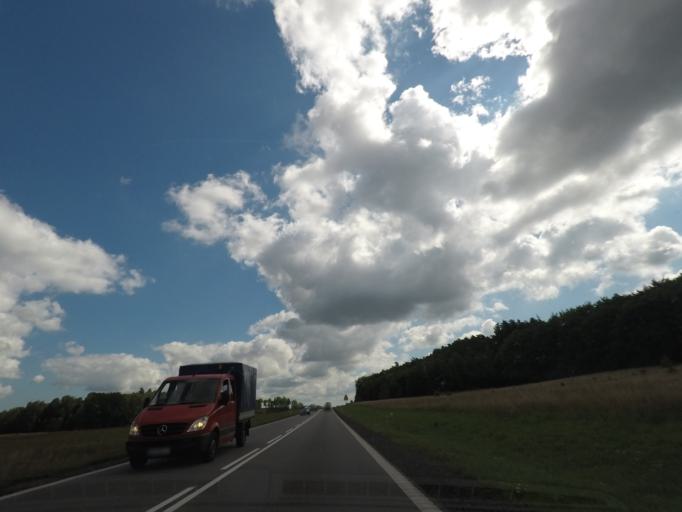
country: PL
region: Pomeranian Voivodeship
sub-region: Powiat wejherowski
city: Leczyce
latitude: 54.5742
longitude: 17.8739
